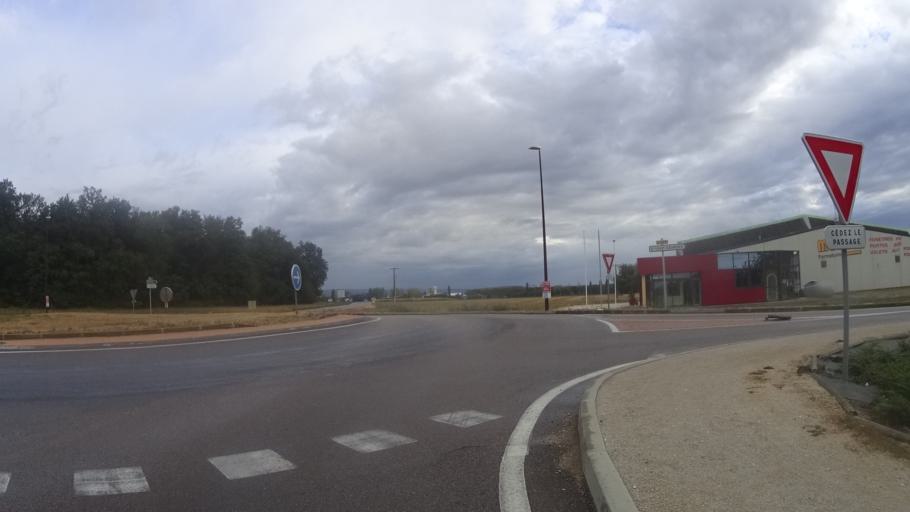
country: FR
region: Bourgogne
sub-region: Departement de Saone-et-Loire
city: Demigny
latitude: 46.9593
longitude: 4.9041
